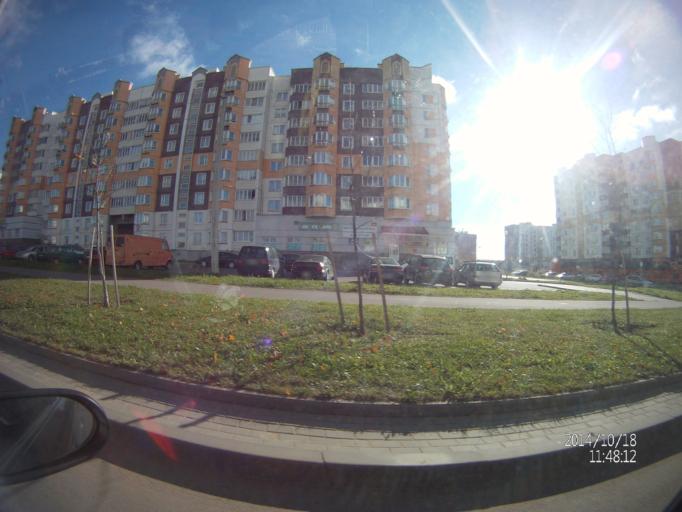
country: BY
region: Minsk
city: Novoye Medvezhino
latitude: 53.8780
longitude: 27.4816
